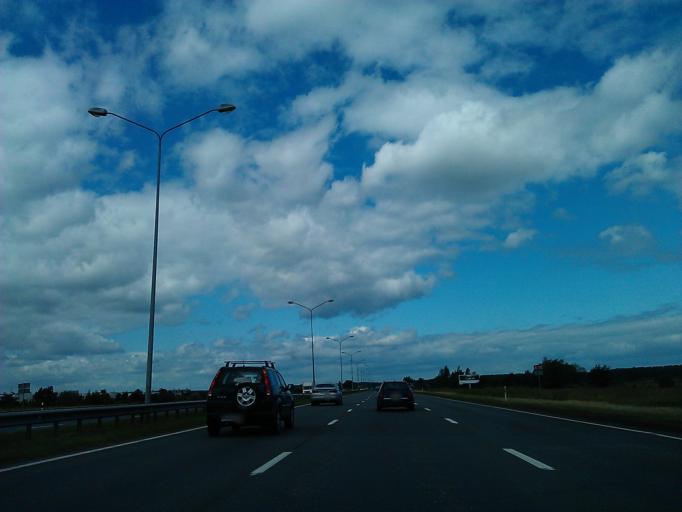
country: LV
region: Babite
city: Pinki
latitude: 56.9566
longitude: 23.9115
